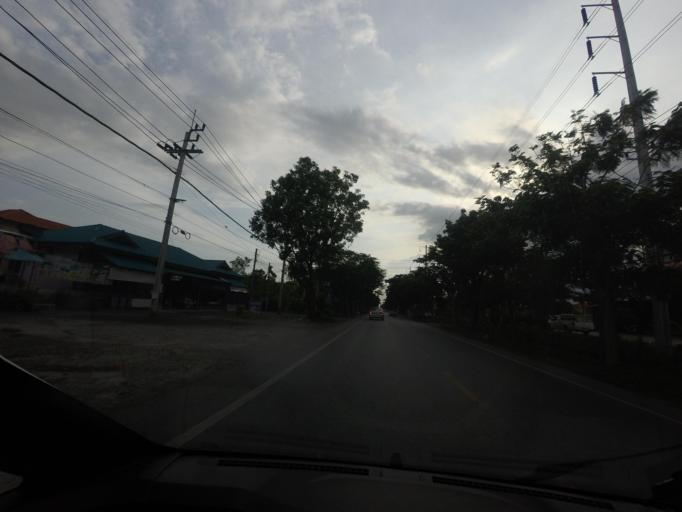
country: TH
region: Bangkok
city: Nong Chok
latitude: 13.8591
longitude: 100.8481
